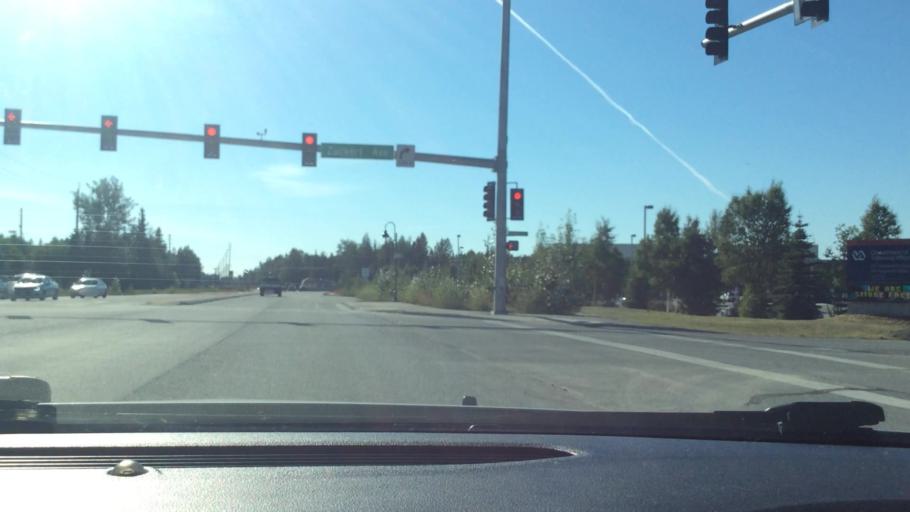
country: US
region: Alaska
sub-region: Anchorage Municipality
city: Elmendorf Air Force Base
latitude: 61.2312
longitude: -149.7410
